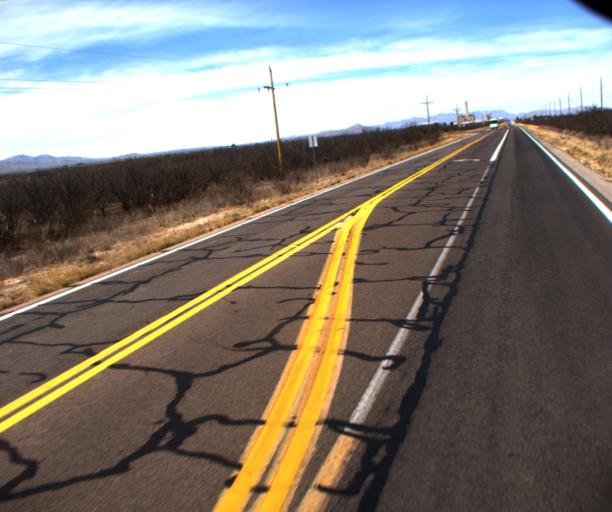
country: US
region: Arizona
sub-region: Cochise County
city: Willcox
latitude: 32.0344
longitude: -109.8781
